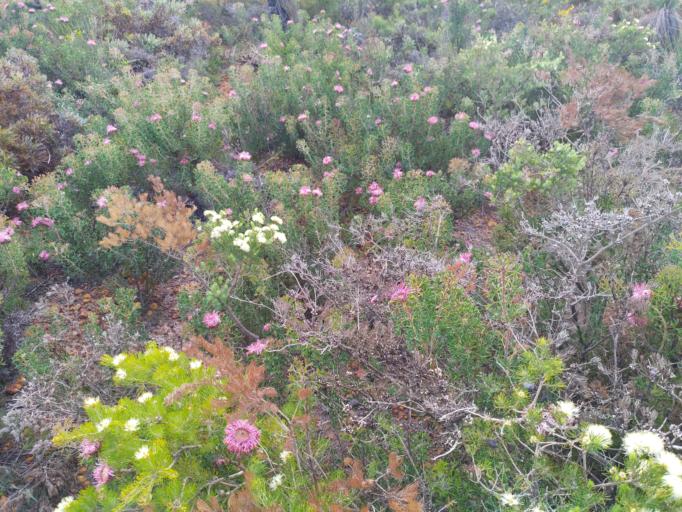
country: AU
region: Western Australia
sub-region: Dandaragan
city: Jurien Bay
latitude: -30.1495
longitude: 115.1218
